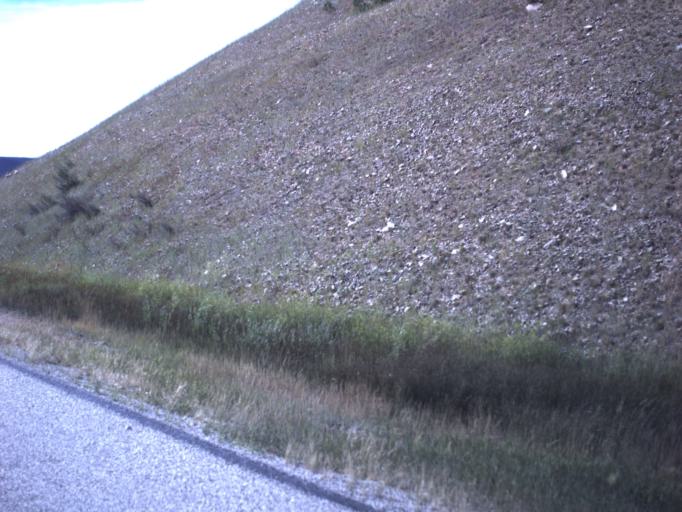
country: US
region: Utah
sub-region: Wasatch County
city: Heber
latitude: 40.2830
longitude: -111.2362
